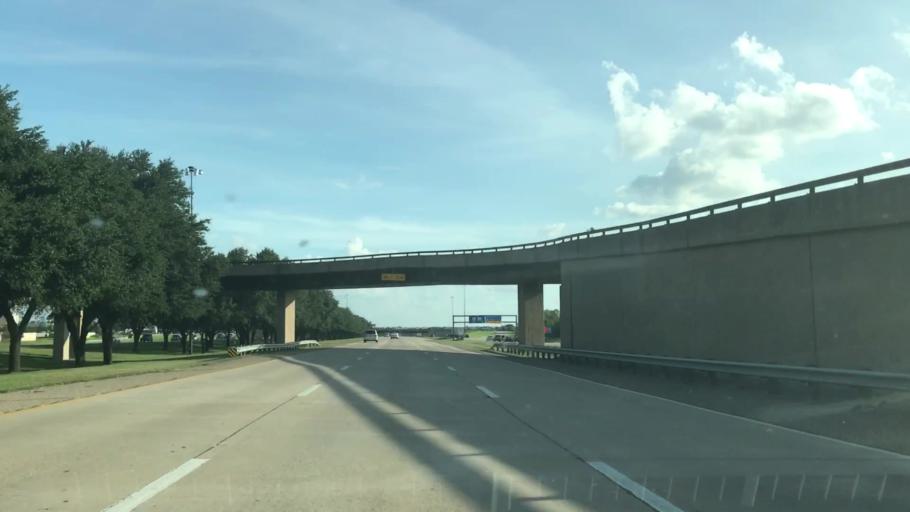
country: US
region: Texas
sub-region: Tarrant County
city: Euless
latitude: 32.8581
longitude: -97.0409
